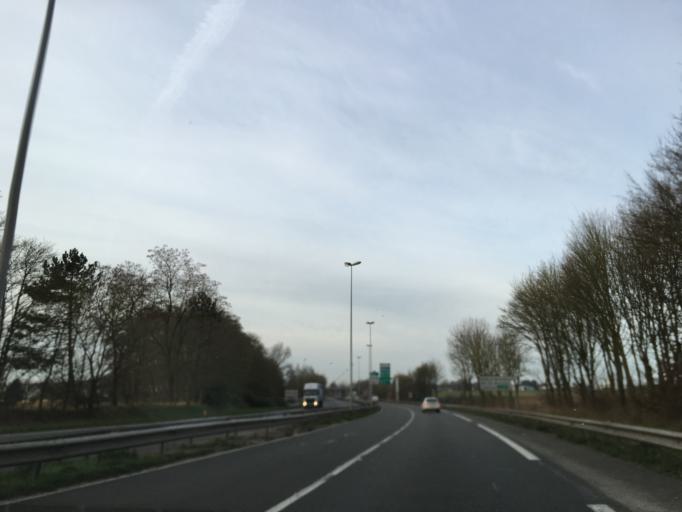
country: FR
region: Nord-Pas-de-Calais
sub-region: Departement du Pas-de-Calais
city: Saint-Nicolas
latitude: 50.3087
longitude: 2.7927
